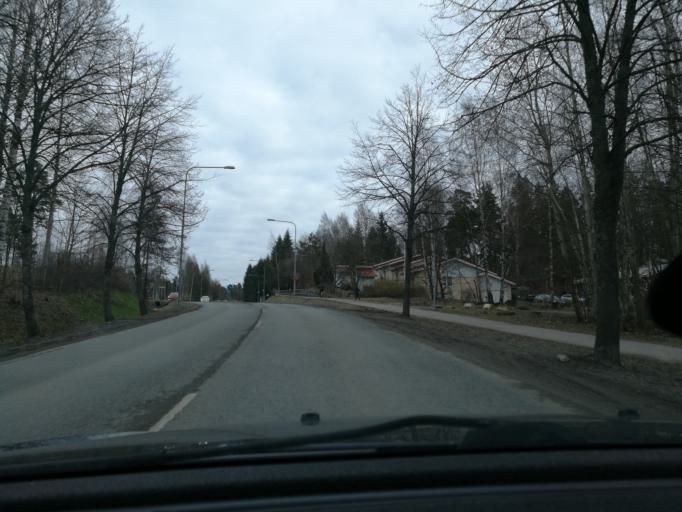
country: FI
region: Uusimaa
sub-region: Helsinki
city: Vantaa
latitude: 60.2851
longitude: 25.0612
